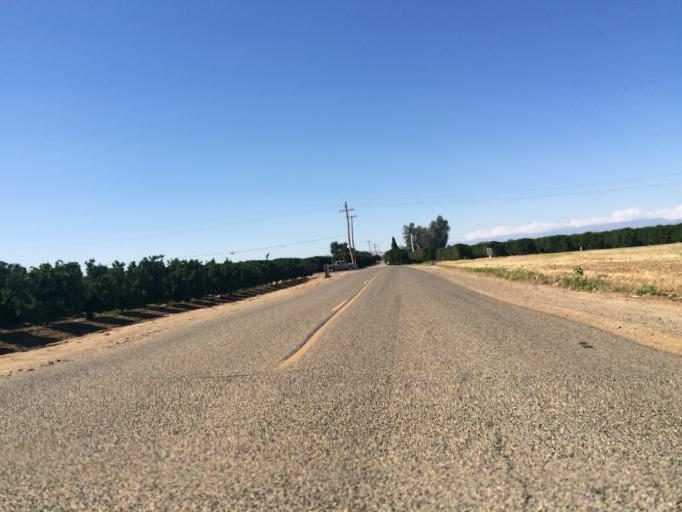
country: US
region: California
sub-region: Fresno County
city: Tarpey Village
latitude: 36.7929
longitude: -119.6279
